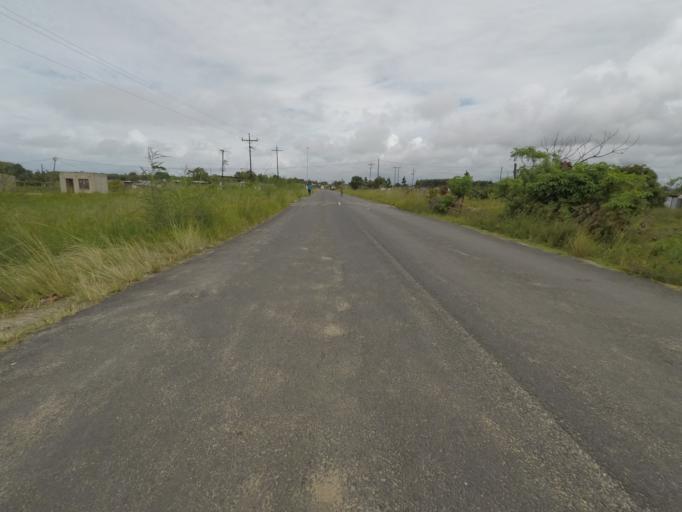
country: ZA
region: KwaZulu-Natal
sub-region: uThungulu District Municipality
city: eSikhawini
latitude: -28.9104
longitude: 31.8679
